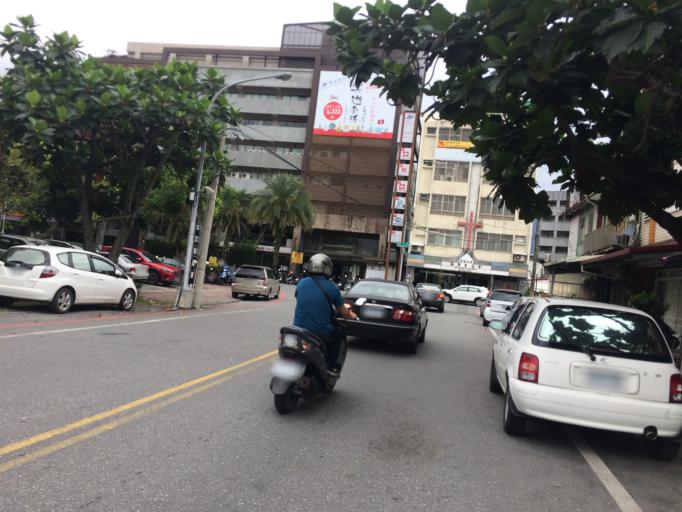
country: TW
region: Taiwan
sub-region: Hualien
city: Hualian
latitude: 23.9847
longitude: 121.6067
